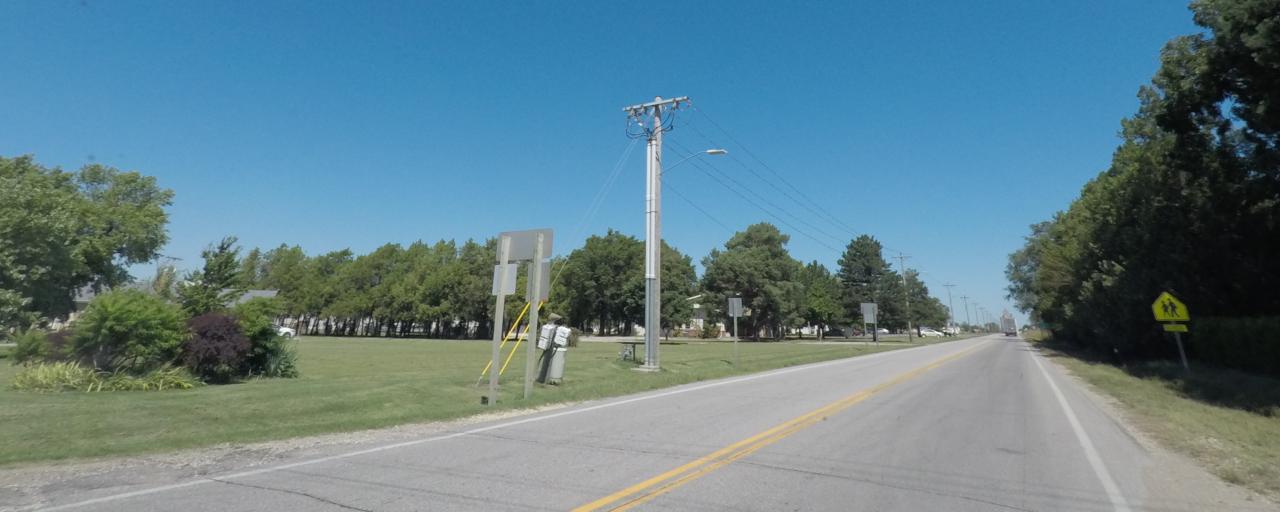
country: US
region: Kansas
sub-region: Sumner County
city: Wellington
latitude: 37.2896
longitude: -97.3943
